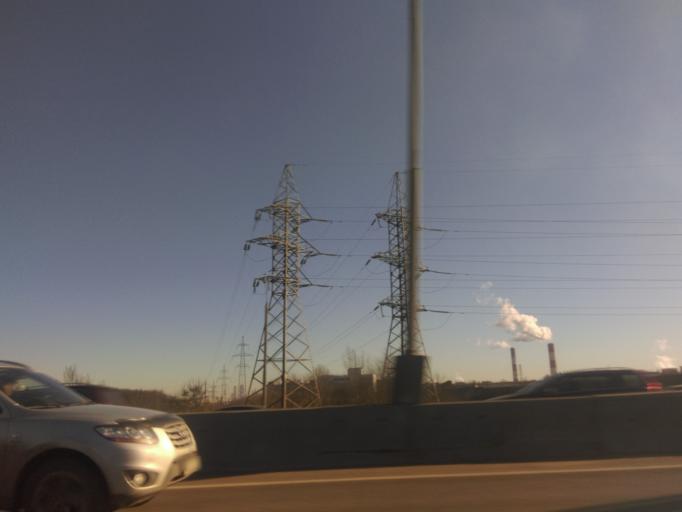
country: RU
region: Moskovskaya
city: Zarech'ye
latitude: 55.6918
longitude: 37.4119
